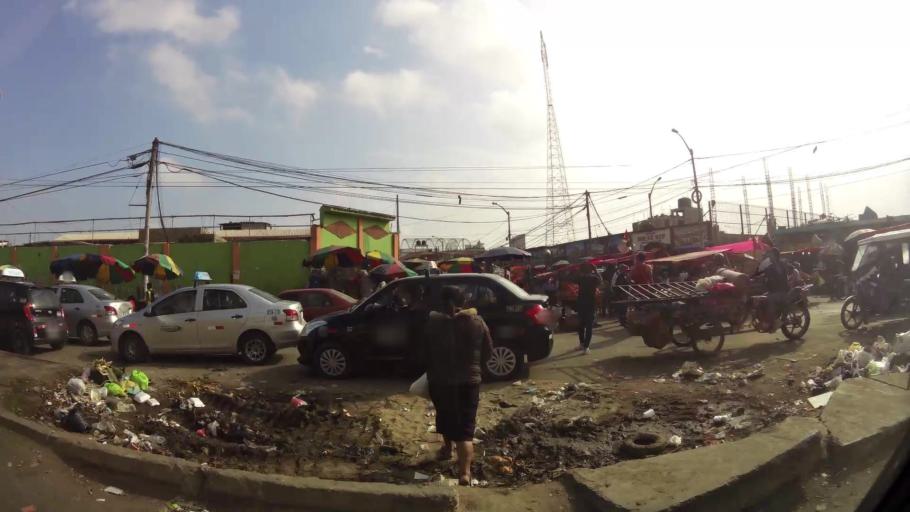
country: PE
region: La Libertad
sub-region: Provincia de Trujillo
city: Trujillo
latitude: -8.1108
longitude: -79.0199
